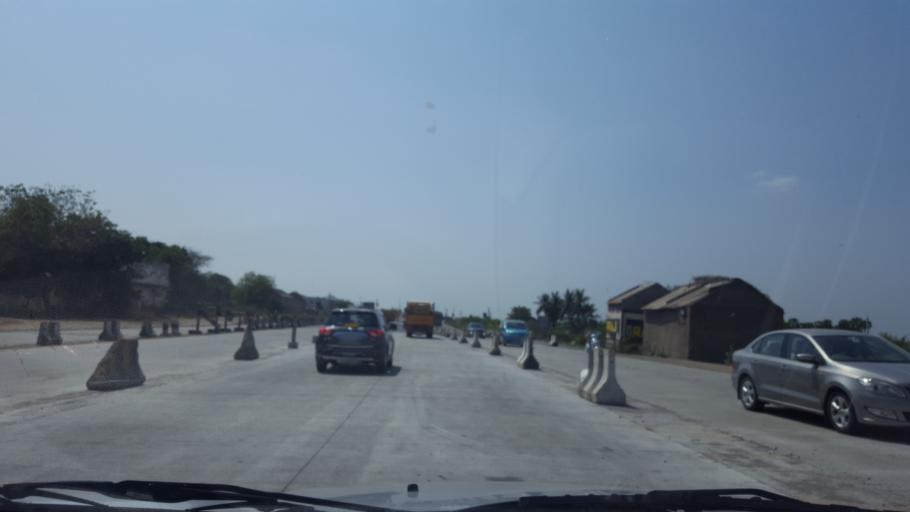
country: IN
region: Andhra Pradesh
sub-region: Prakasam
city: Addanki
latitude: 15.7609
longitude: 80.0317
